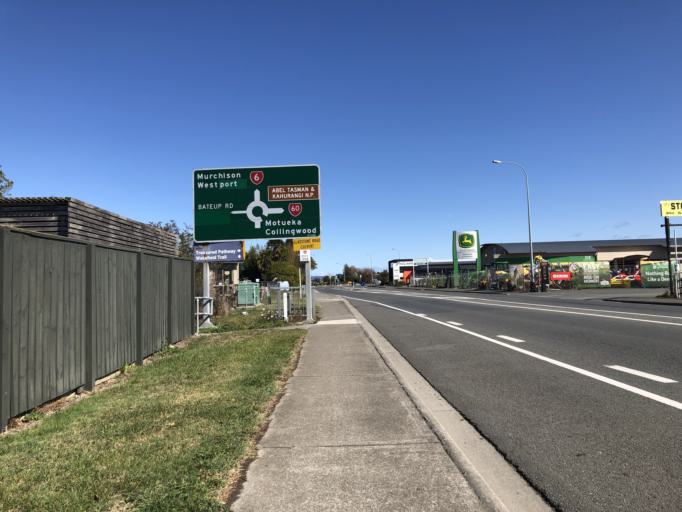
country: NZ
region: Tasman
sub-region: Tasman District
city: Richmond
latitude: -41.3443
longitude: 173.1696
